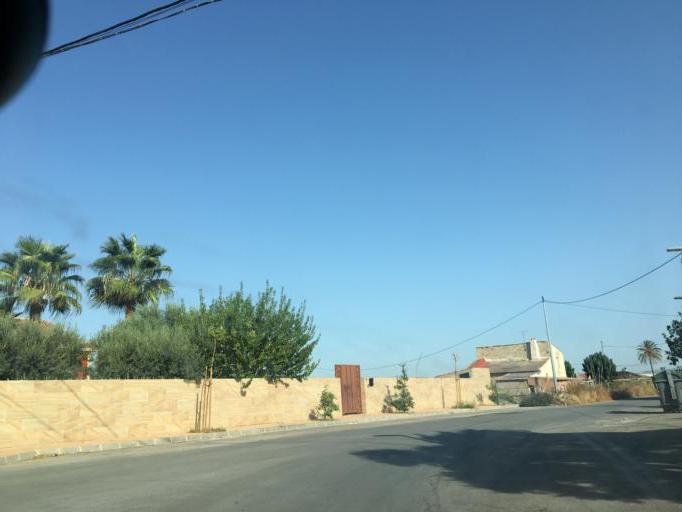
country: ES
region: Murcia
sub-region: Murcia
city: Santomera
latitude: 38.0338
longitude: -1.0705
